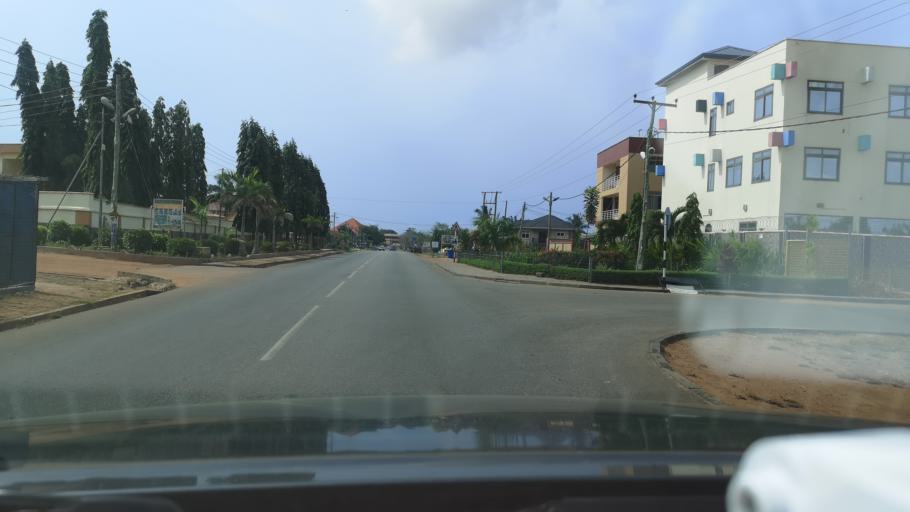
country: GH
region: Greater Accra
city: Tema
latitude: 5.6723
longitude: -0.0288
